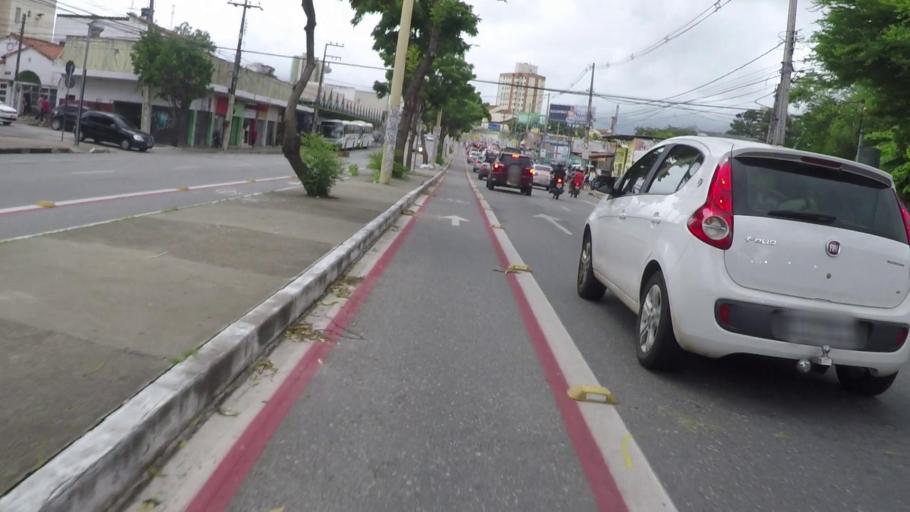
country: BR
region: Ceara
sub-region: Fortaleza
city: Fortaleza
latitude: -3.7380
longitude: -38.5266
